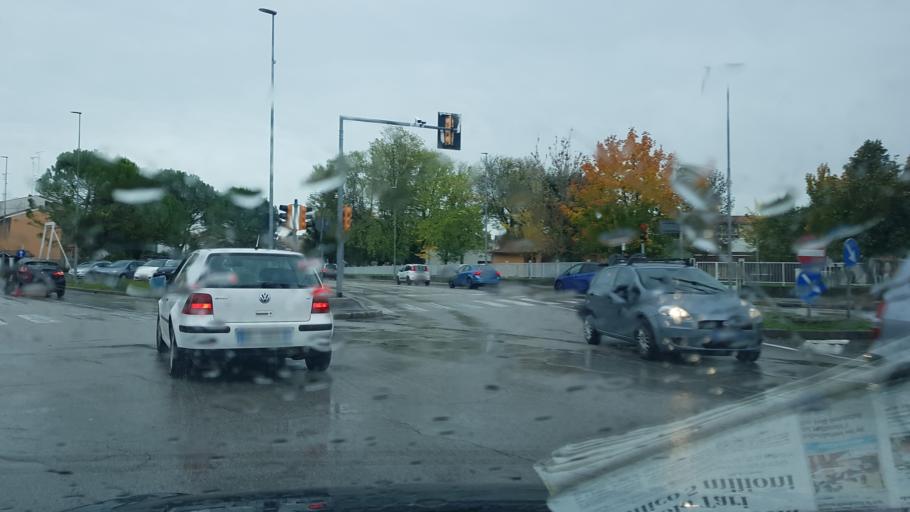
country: IT
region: Friuli Venezia Giulia
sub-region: Provincia di Gorizia
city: Ronchi dei Legionari
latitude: 45.8270
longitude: 13.5046
